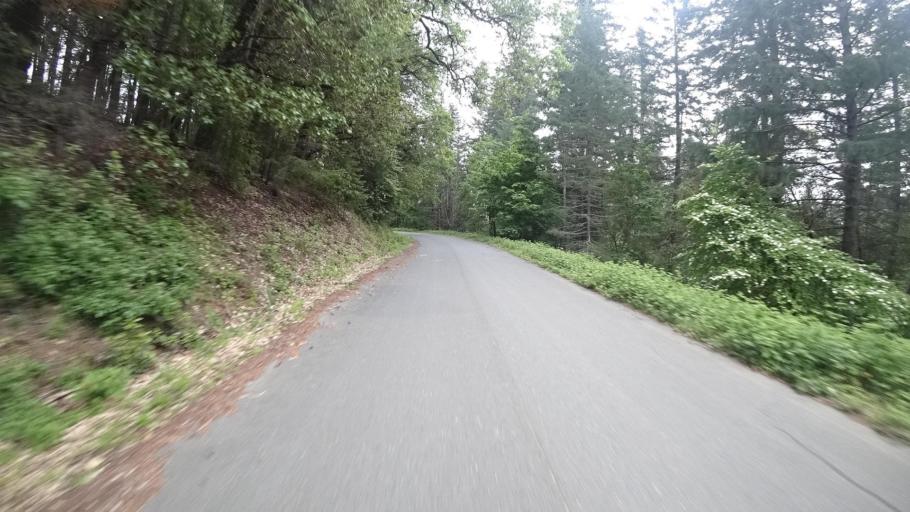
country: US
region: California
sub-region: Humboldt County
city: Willow Creek
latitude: 41.1185
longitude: -123.7361
